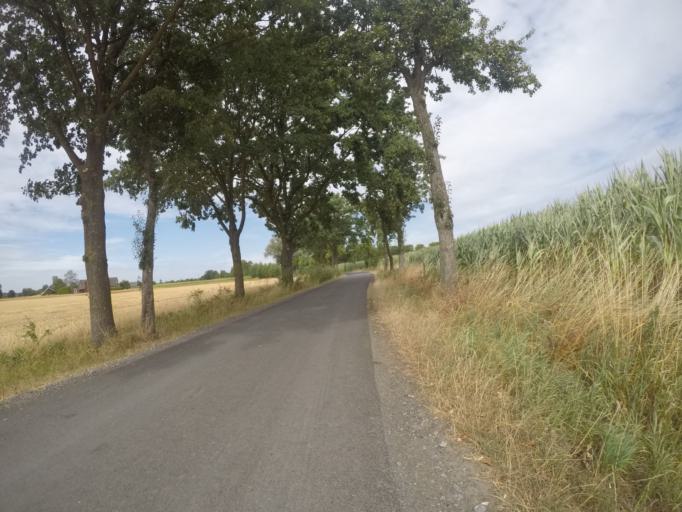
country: DE
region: North Rhine-Westphalia
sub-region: Regierungsbezirk Dusseldorf
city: Bocholt
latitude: 51.8533
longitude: 6.5664
